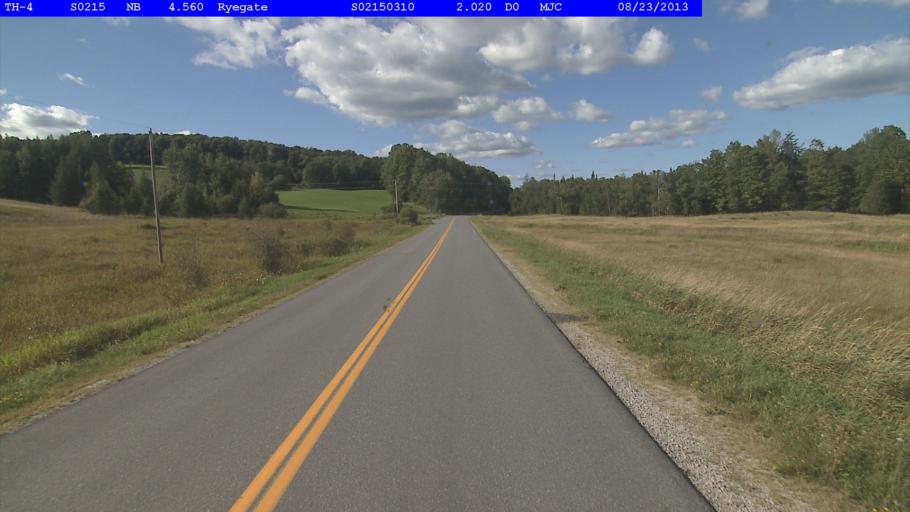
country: US
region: New Hampshire
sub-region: Grafton County
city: Woodsville
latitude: 44.2700
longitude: -72.1734
